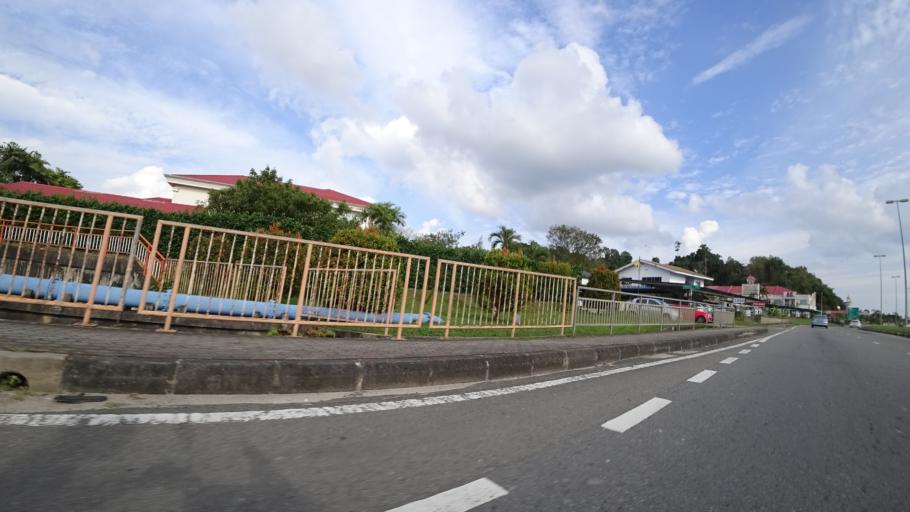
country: BN
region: Brunei and Muara
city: Bandar Seri Begawan
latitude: 4.8727
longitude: 114.8617
